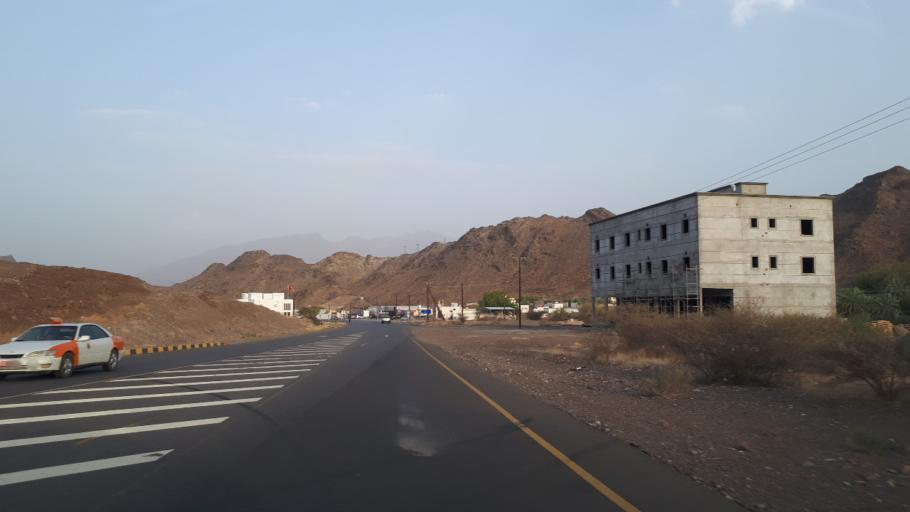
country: OM
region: Al Batinah
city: Rustaq
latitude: 23.4270
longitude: 57.2853
